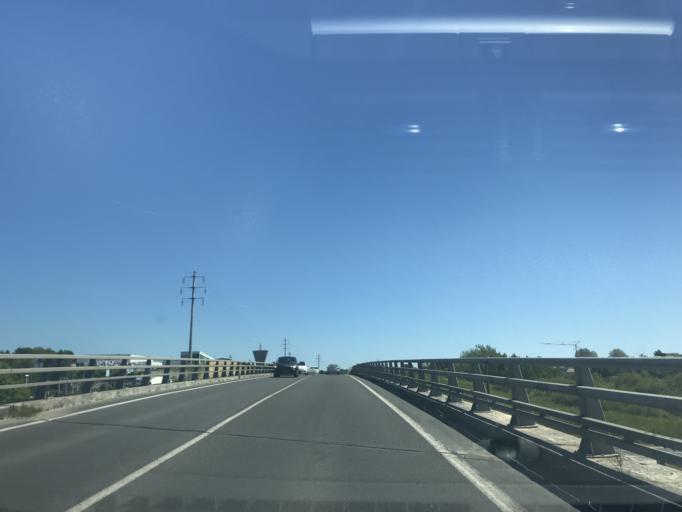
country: FR
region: Poitou-Charentes
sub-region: Departement de la Charente-Maritime
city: Royan
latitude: 45.6309
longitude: -1.0071
